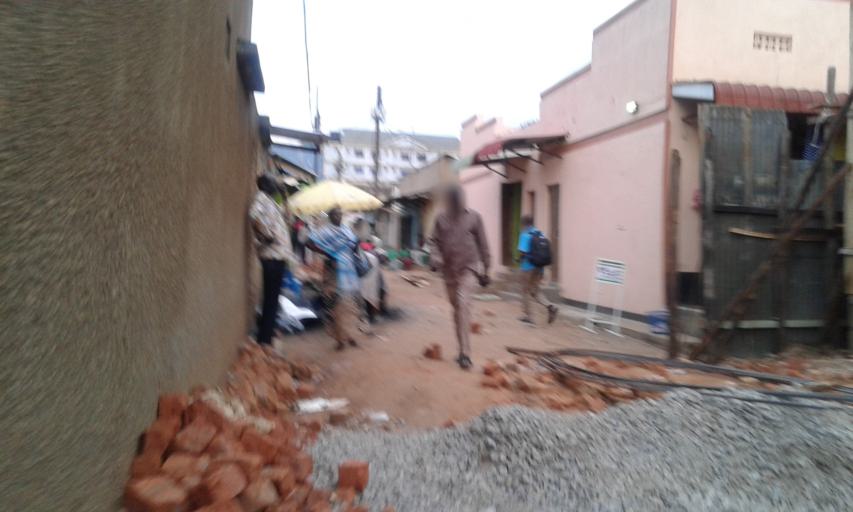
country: UG
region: Eastern Region
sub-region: Mbale District
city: Mbale
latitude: 1.0748
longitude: 34.1778
